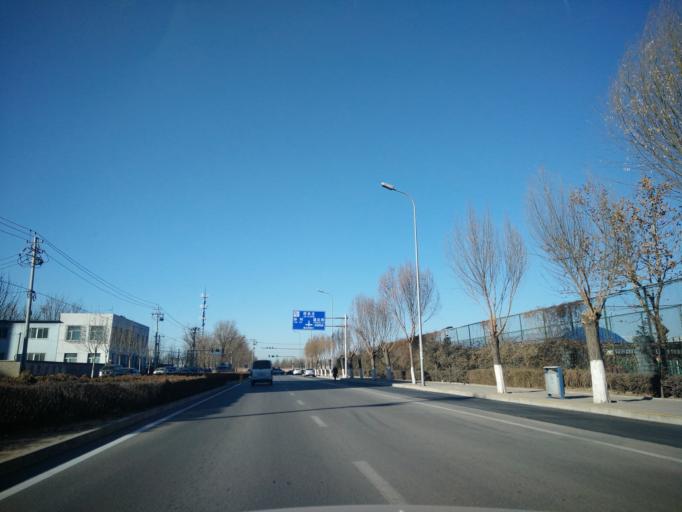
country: CN
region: Beijing
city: Xingfeng
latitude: 39.7085
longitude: 116.3946
